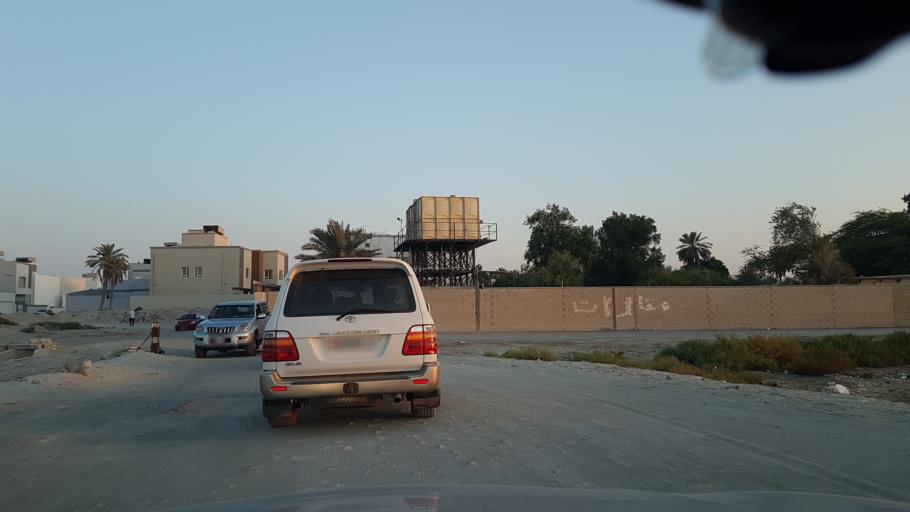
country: BH
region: Manama
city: Jidd Hafs
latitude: 26.2362
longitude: 50.5054
